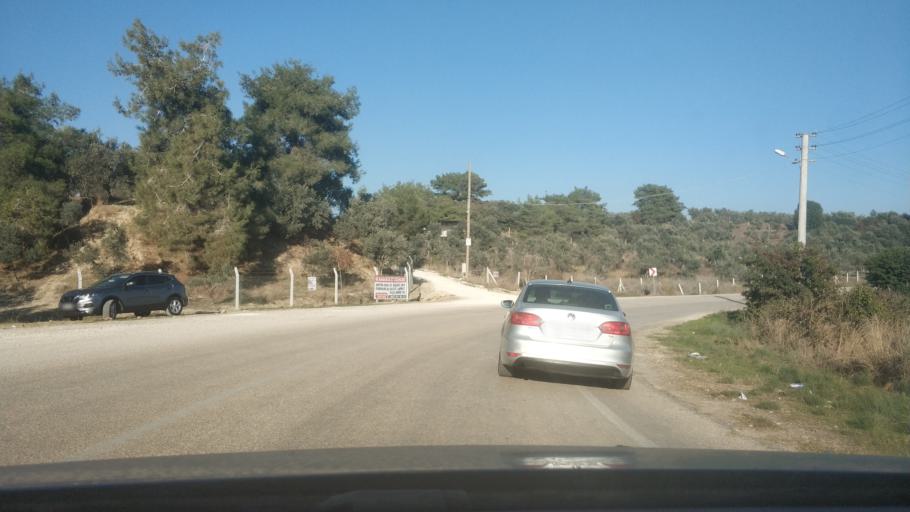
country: TR
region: Adana
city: Adana
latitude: 37.1027
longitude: 35.2918
